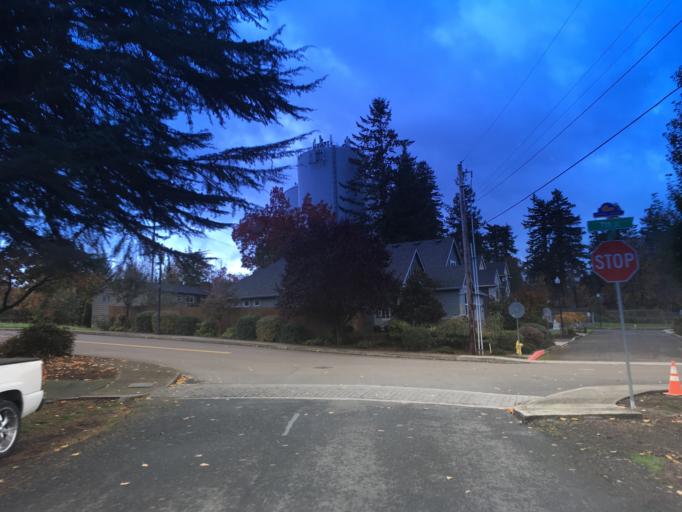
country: US
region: Oregon
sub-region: Multnomah County
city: Fairview
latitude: 45.5348
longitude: -122.4398
